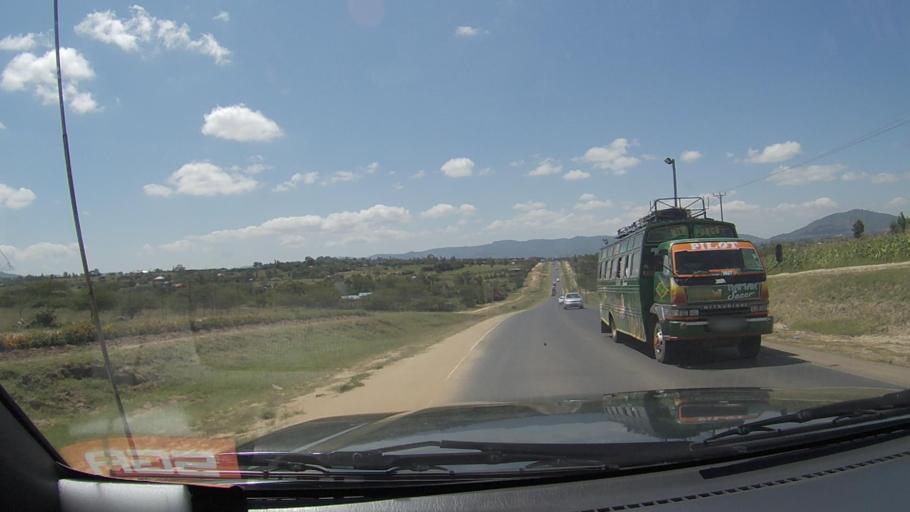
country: KE
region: Machakos
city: Machakos
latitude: -1.5309
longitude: 37.2022
